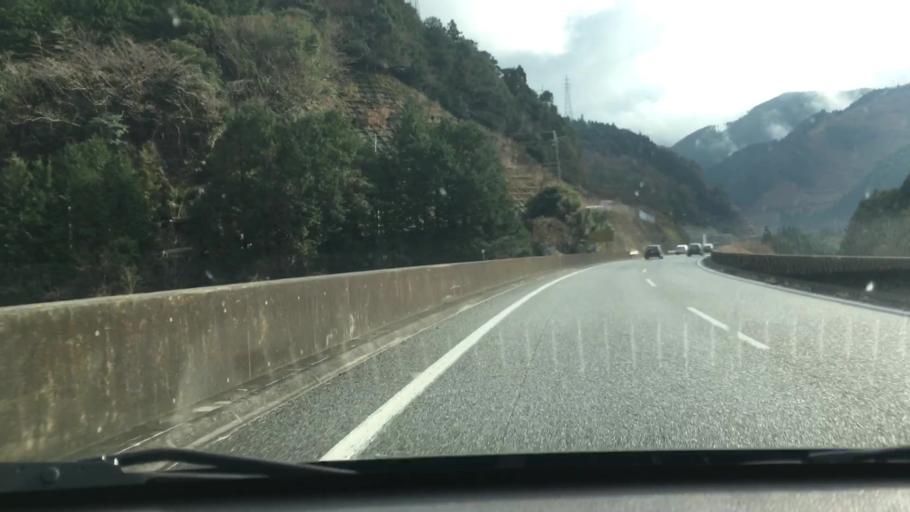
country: JP
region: Kumamoto
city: Yatsushiro
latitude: 32.4098
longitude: 130.6965
